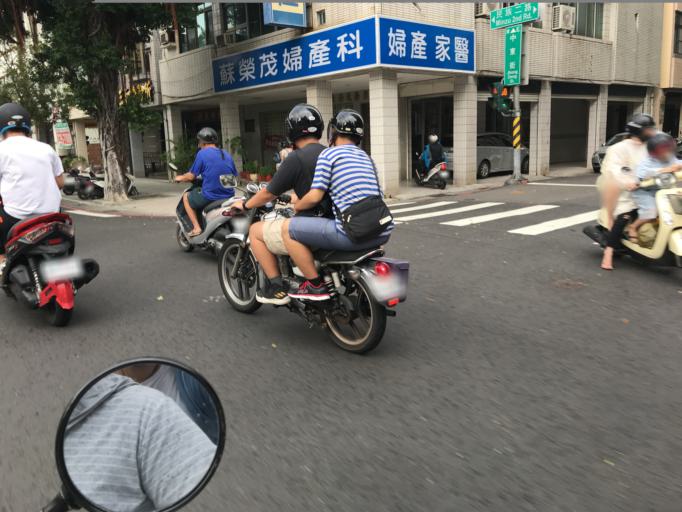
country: TW
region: Kaohsiung
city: Kaohsiung
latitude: 22.6326
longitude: 120.3136
